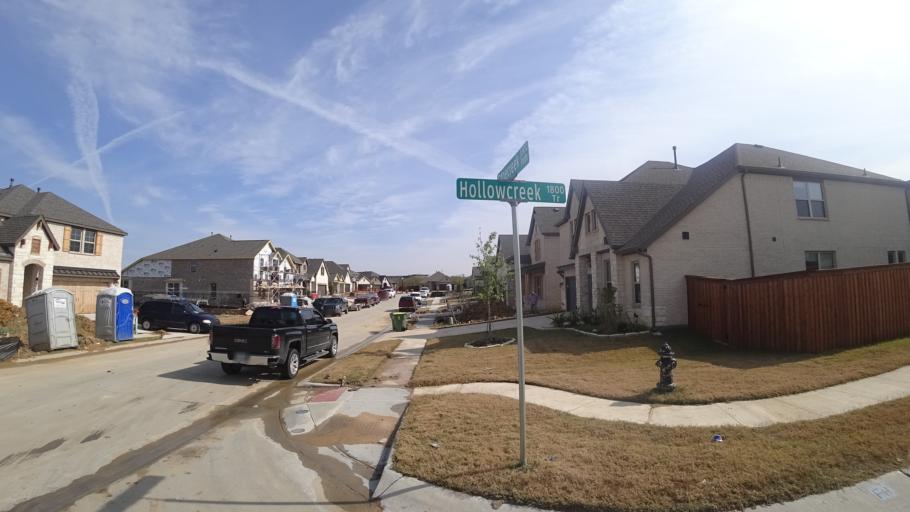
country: US
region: Texas
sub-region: Denton County
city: The Colony
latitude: 33.0494
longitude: -96.8825
